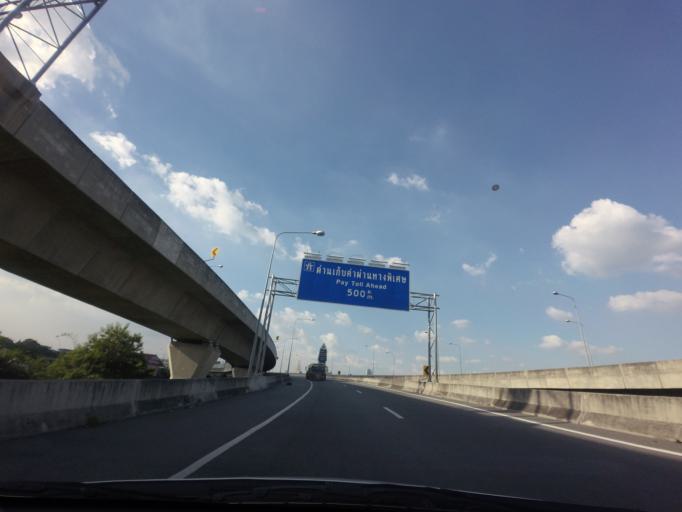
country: TH
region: Samut Prakan
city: Phra Pradaeng
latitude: 13.6407
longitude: 100.5497
